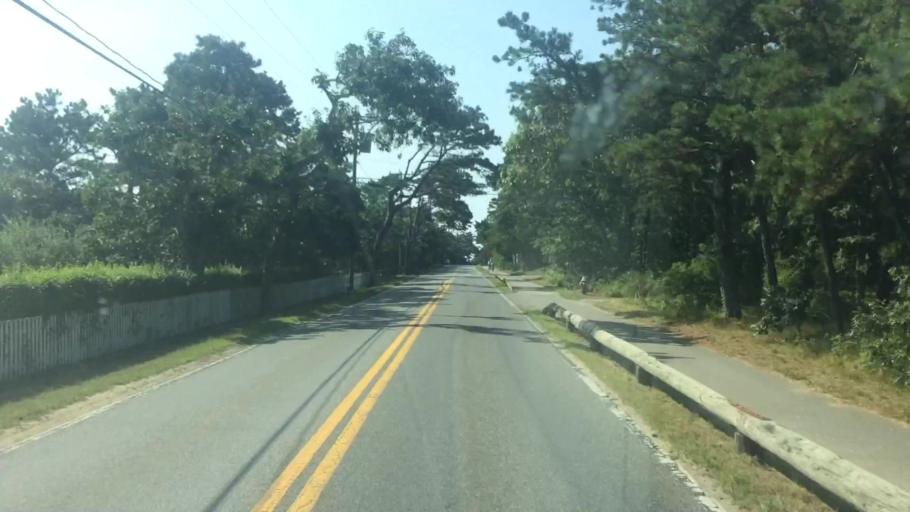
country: US
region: Massachusetts
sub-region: Dukes County
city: Oak Bluffs
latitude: 41.4433
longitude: -70.5547
